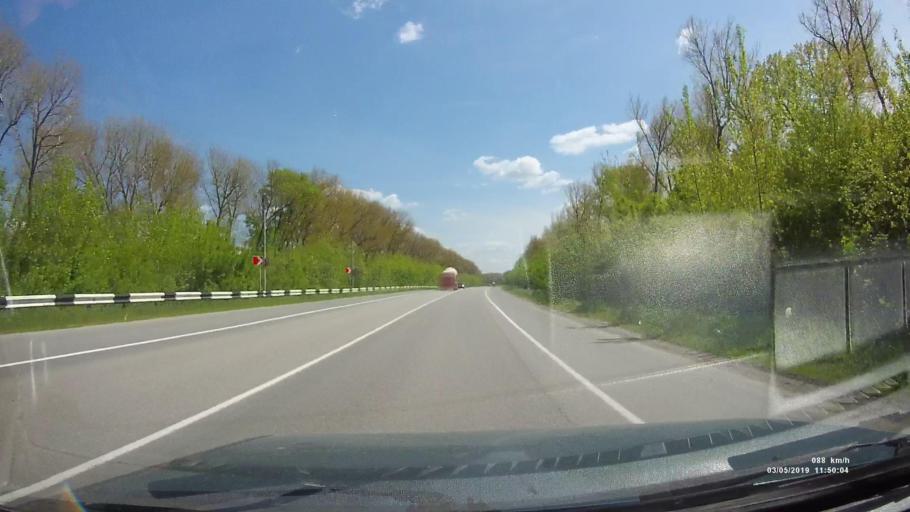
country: RU
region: Rostov
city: Starocherkasskaya
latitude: 47.1555
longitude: 40.1895
